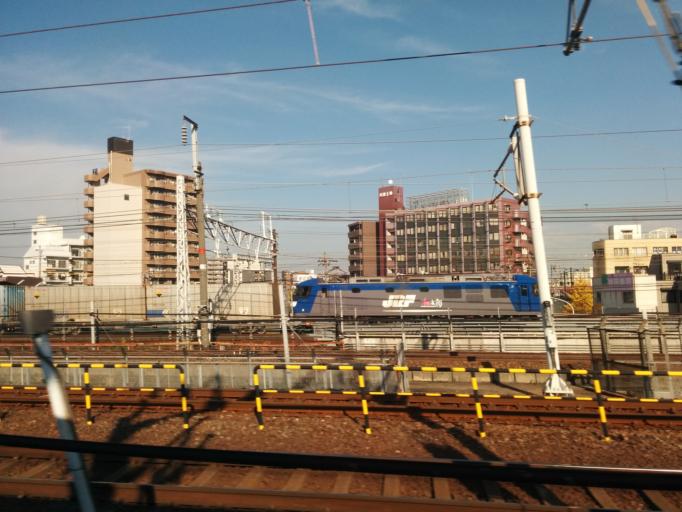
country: JP
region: Aichi
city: Nagoya-shi
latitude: 35.1828
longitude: 136.8733
